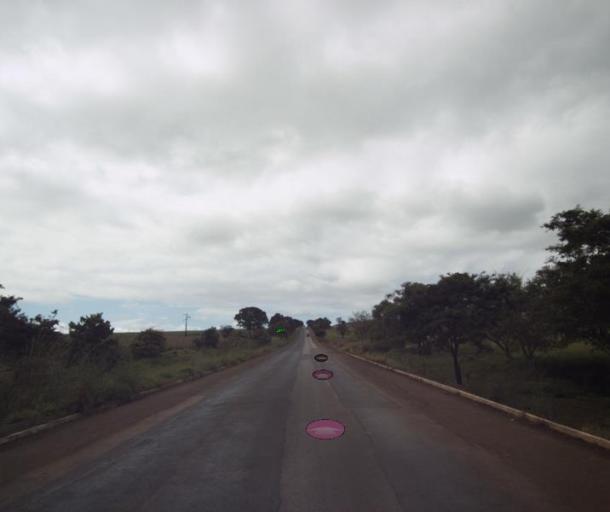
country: BR
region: Goias
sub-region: Barro Alto
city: Barro Alto
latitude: -15.0139
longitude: -48.9000
